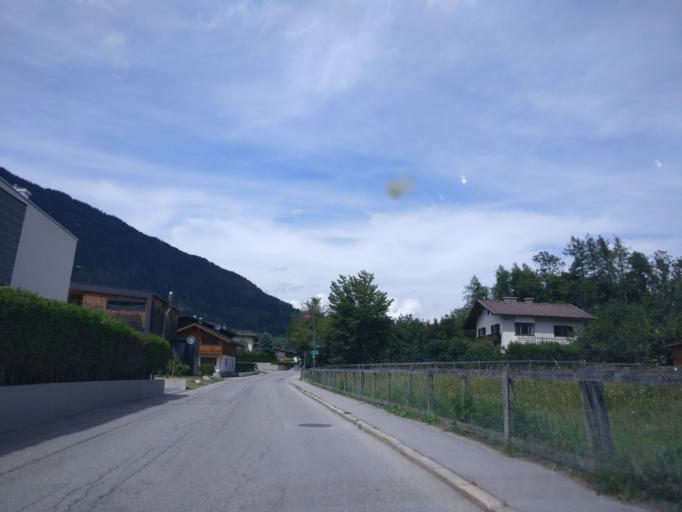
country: AT
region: Tyrol
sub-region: Politischer Bezirk Innsbruck Land
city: Mieders
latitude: 47.1650
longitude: 11.3797
